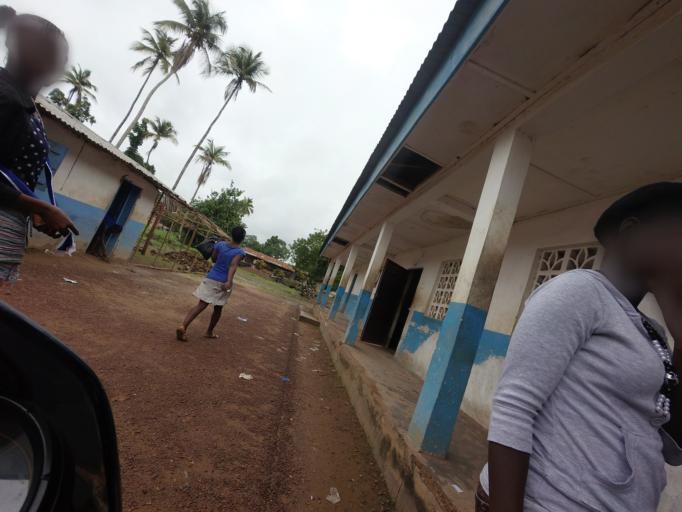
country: SL
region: Northern Province
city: Kambia
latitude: 9.1258
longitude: -12.9154
